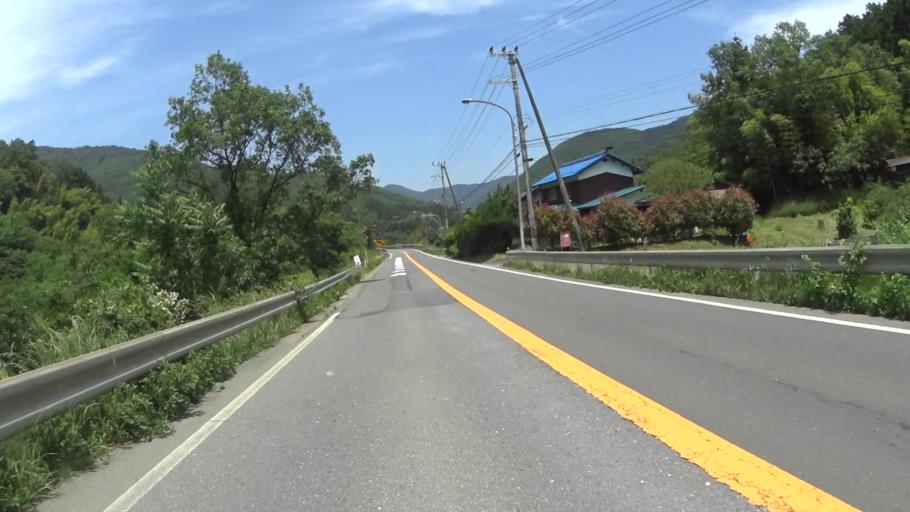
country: JP
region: Kyoto
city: Ayabe
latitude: 35.2050
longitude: 135.2830
